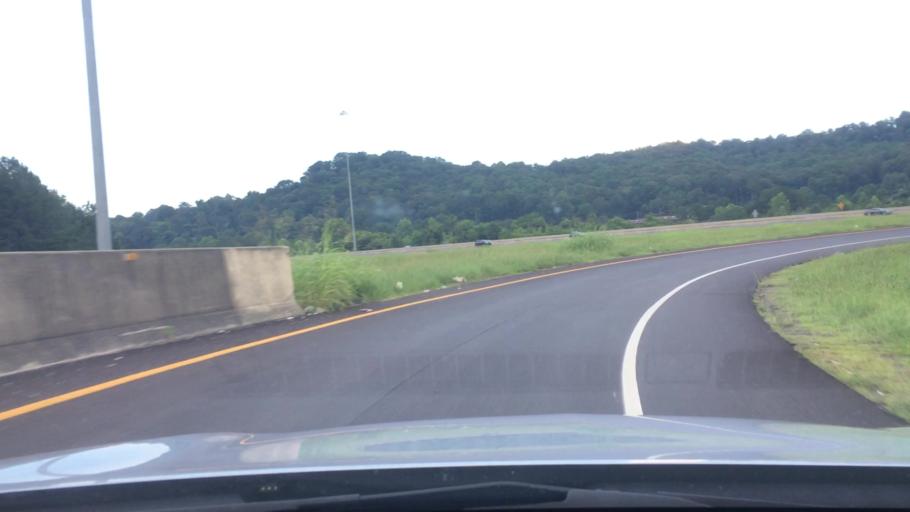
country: US
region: Alabama
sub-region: Jefferson County
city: Leeds
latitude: 33.5466
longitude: -86.5912
